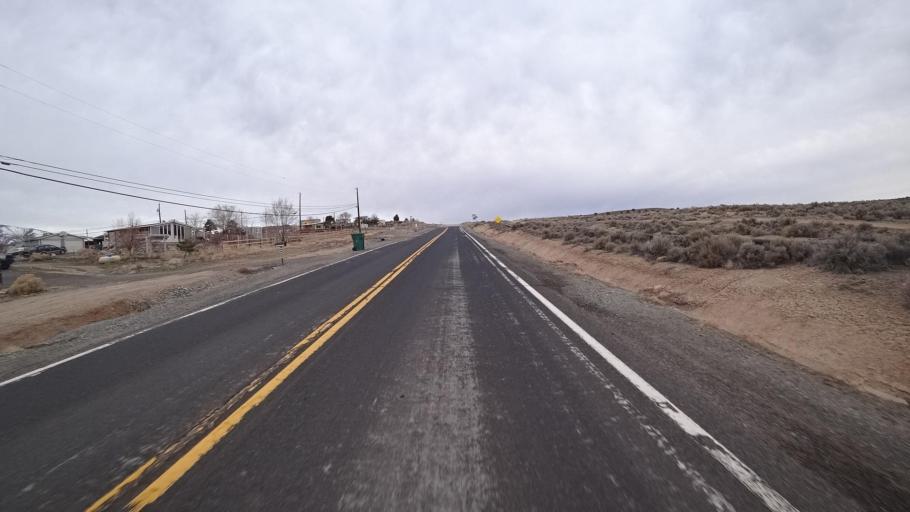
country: US
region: Nevada
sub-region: Washoe County
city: Lemmon Valley
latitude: 39.6766
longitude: -119.8522
